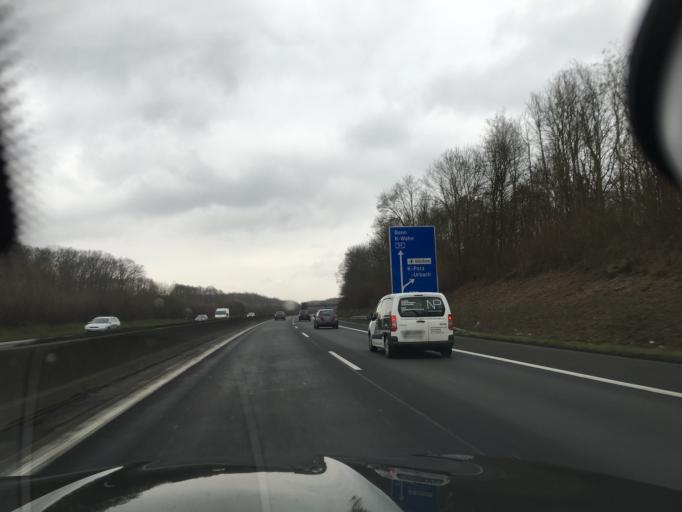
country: DE
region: North Rhine-Westphalia
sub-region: Regierungsbezirk Koln
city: Eil
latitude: 50.8949
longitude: 7.0886
